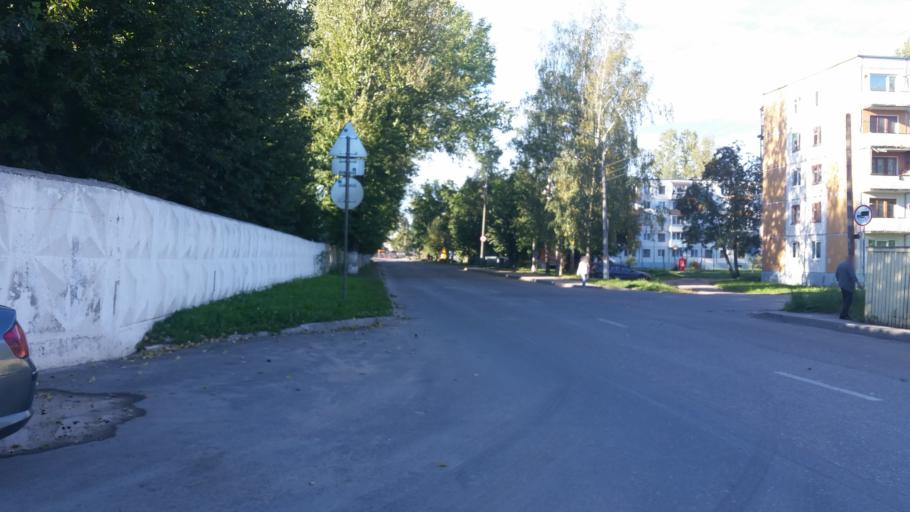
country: BY
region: Vitebsk
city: Vitebsk
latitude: 55.1826
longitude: 30.1874
